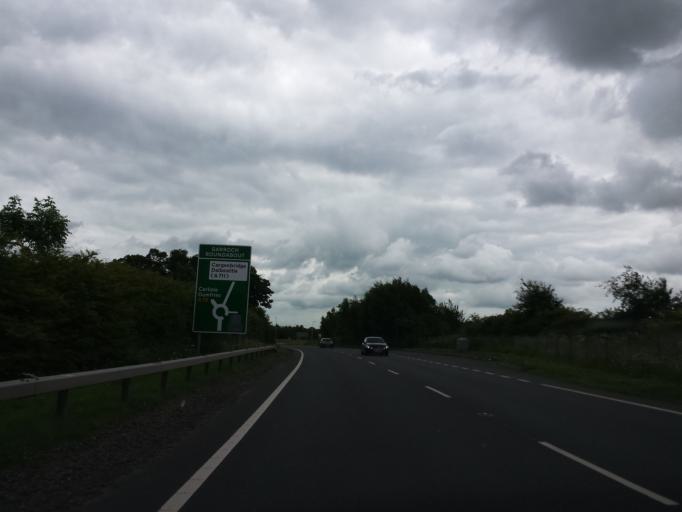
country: GB
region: Scotland
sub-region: Dumfries and Galloway
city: Dumfries
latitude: 55.0612
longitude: -3.6601
